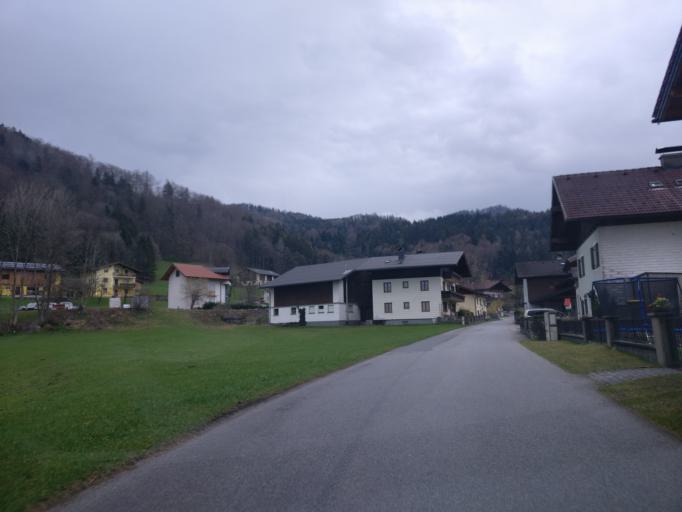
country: AT
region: Salzburg
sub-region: Politischer Bezirk Hallein
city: Golling an der Salzach
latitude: 47.6267
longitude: 13.1727
